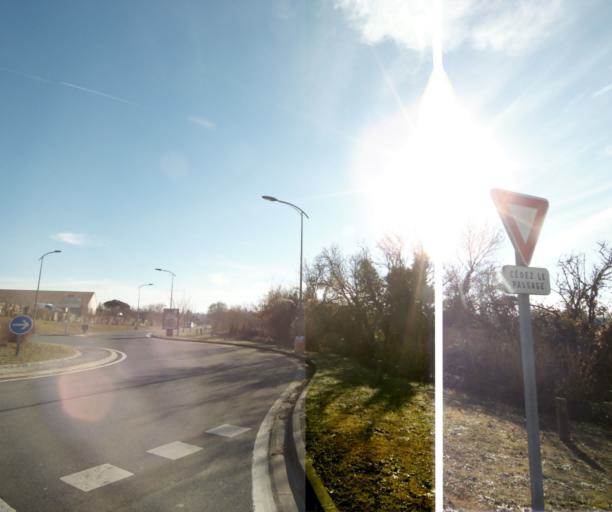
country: FR
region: Poitou-Charentes
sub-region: Departement de la Charente-Maritime
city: Chaniers
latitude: 45.7226
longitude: -0.5680
